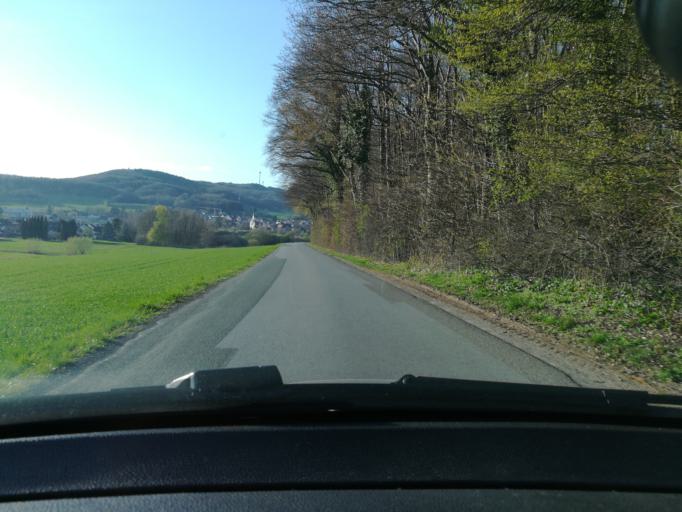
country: DE
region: North Rhine-Westphalia
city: Borgholzhausen
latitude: 52.0968
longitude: 8.3115
